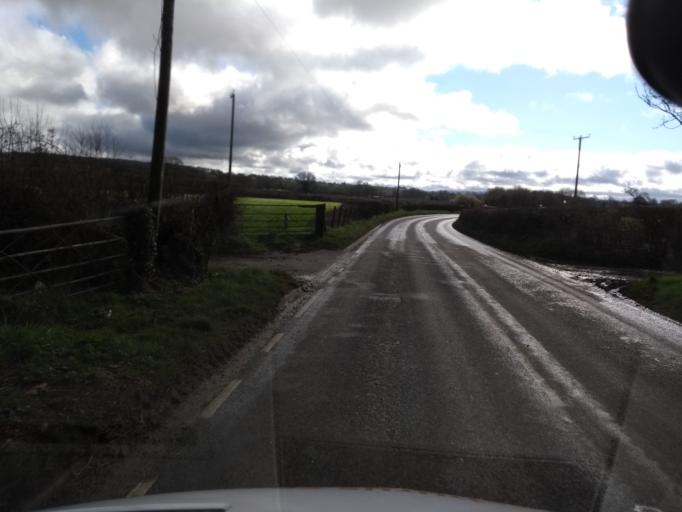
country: GB
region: England
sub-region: Somerset
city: Milborne Port
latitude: 50.9237
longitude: -2.4734
